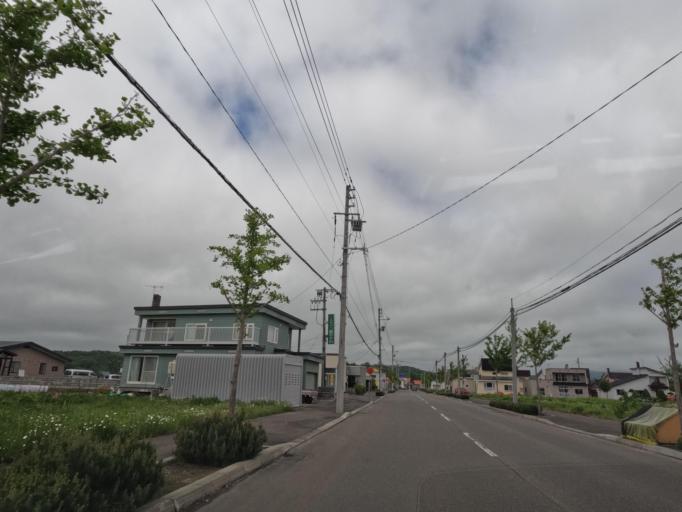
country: JP
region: Hokkaido
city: Tobetsu
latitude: 43.2355
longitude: 141.5142
